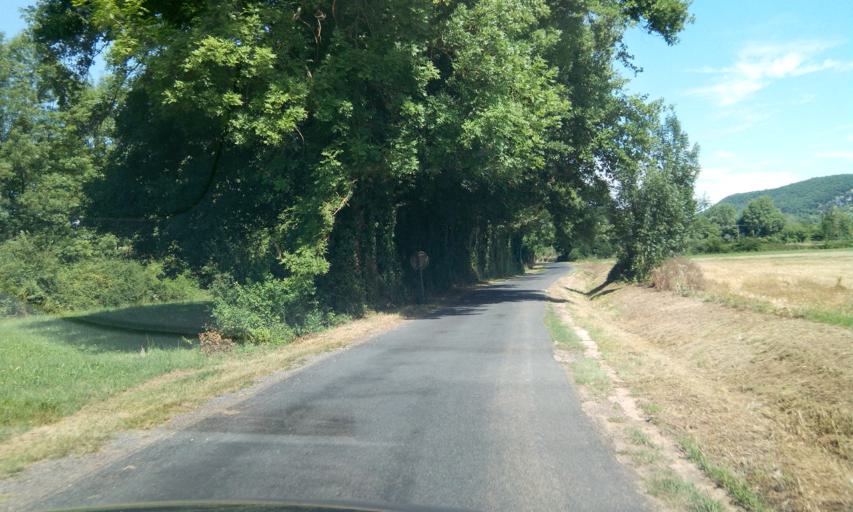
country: FR
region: Midi-Pyrenees
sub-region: Departement du Lot
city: Vayrac
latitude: 44.9389
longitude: 1.6658
